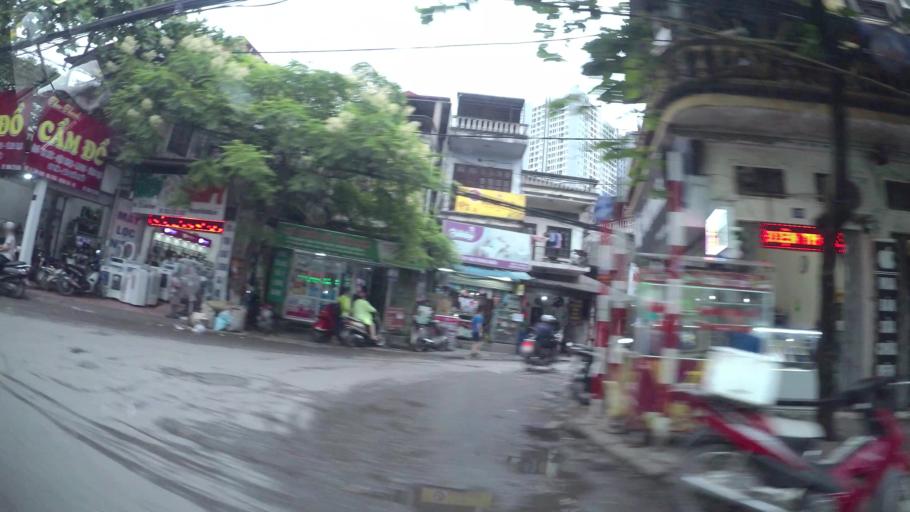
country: VN
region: Ha Noi
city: Hai BaTrung
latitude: 20.9909
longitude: 105.8642
